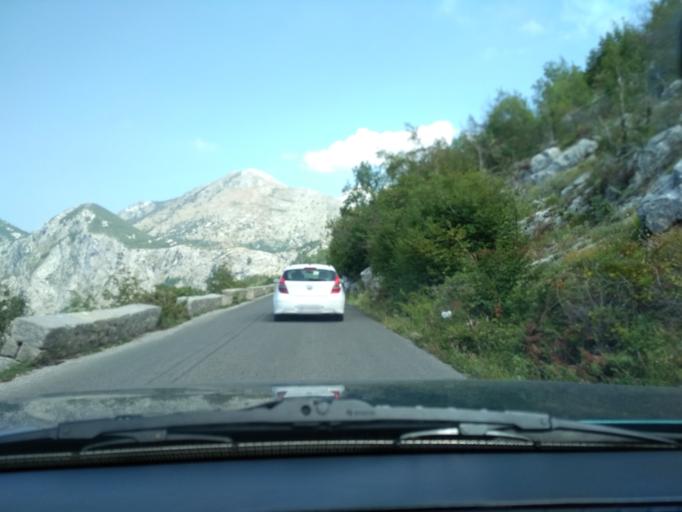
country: ME
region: Kotor
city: Kotor
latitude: 42.4154
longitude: 18.7920
